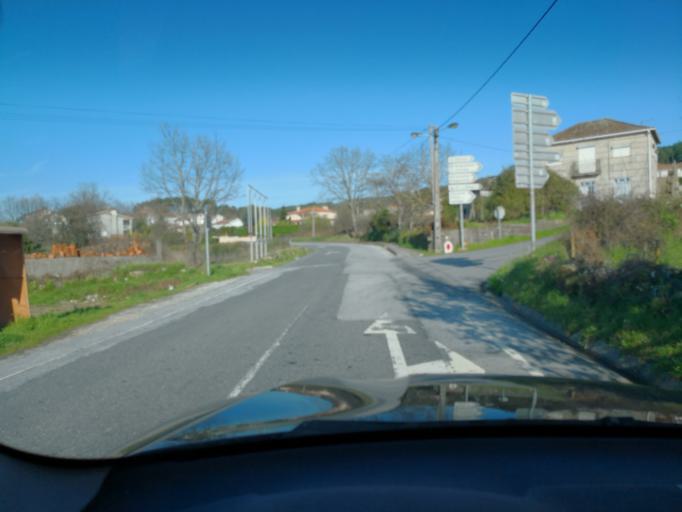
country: PT
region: Vila Real
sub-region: Vila Real
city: Vila Real
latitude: 41.3240
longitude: -7.6798
